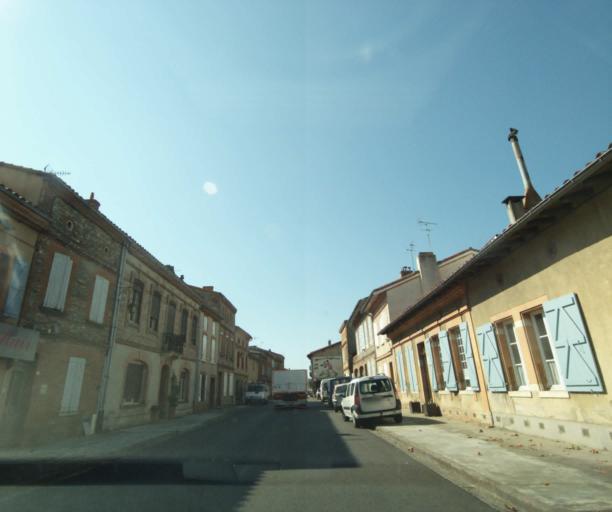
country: FR
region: Midi-Pyrenees
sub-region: Departement de la Haute-Garonne
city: Saint-Sulpice-sur-Leze
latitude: 43.3297
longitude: 1.3222
